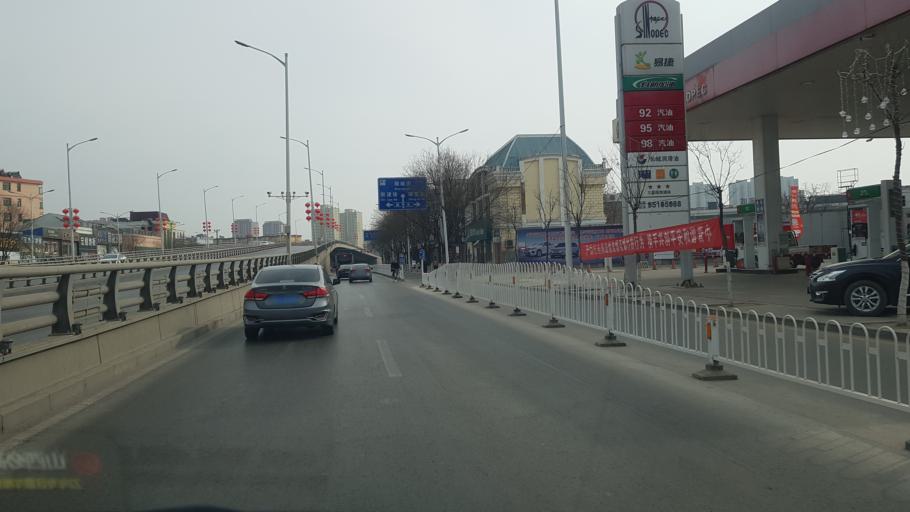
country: CN
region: Shanxi Sheng
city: Yuci
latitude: 37.6915
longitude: 112.7197
